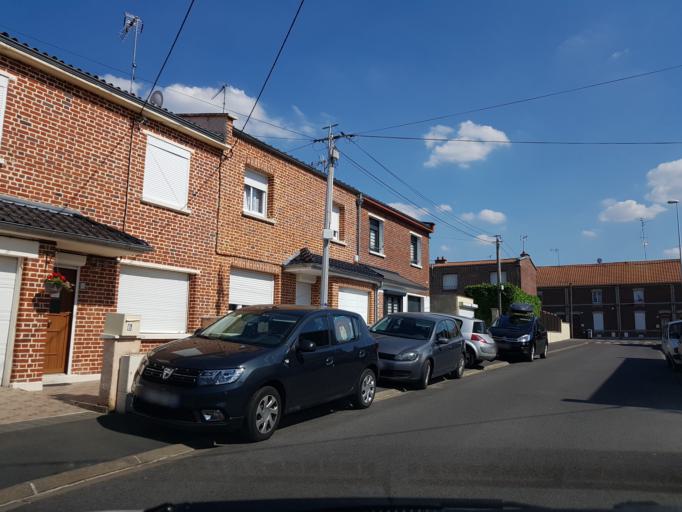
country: FR
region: Nord-Pas-de-Calais
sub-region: Departement du Nord
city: Lourches
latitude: 50.3134
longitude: 3.3396
